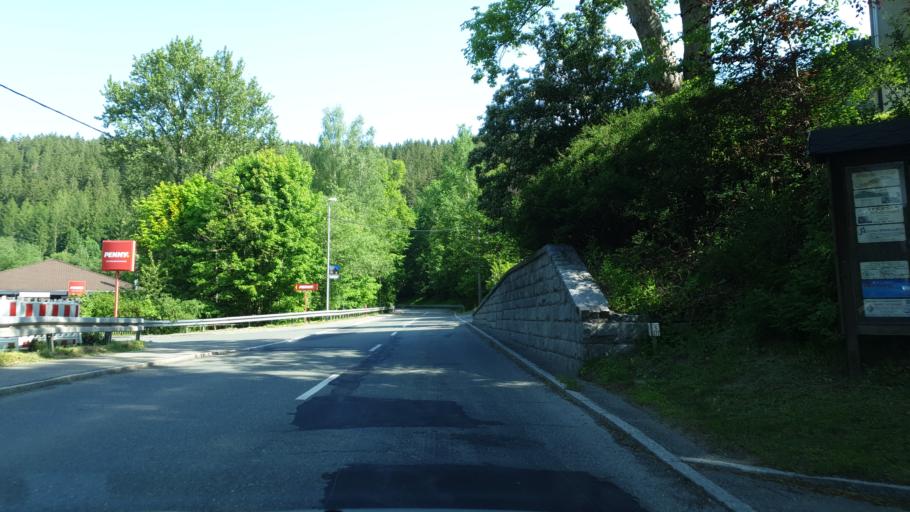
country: DE
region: Saxony
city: Schoenheide
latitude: 50.5061
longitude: 12.5564
